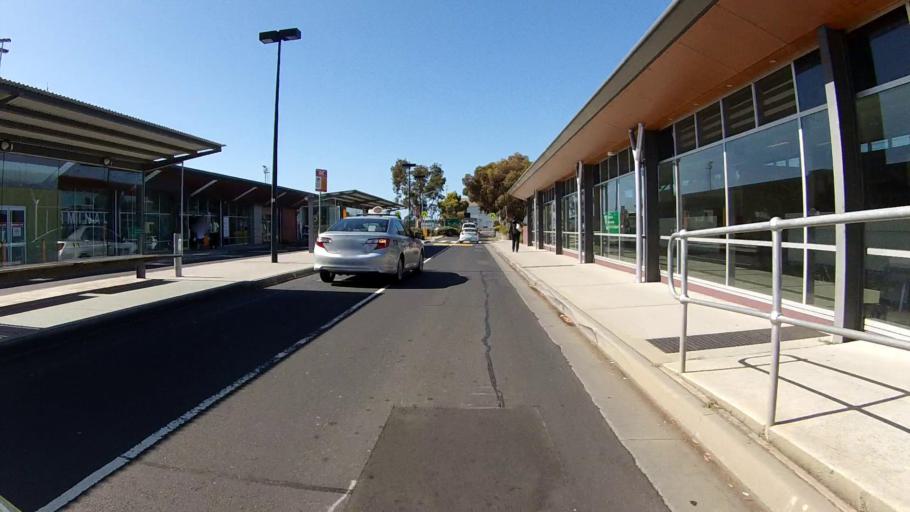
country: AU
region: Tasmania
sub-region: Clarence
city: Seven Mile Beach
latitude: -42.8377
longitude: 147.5056
